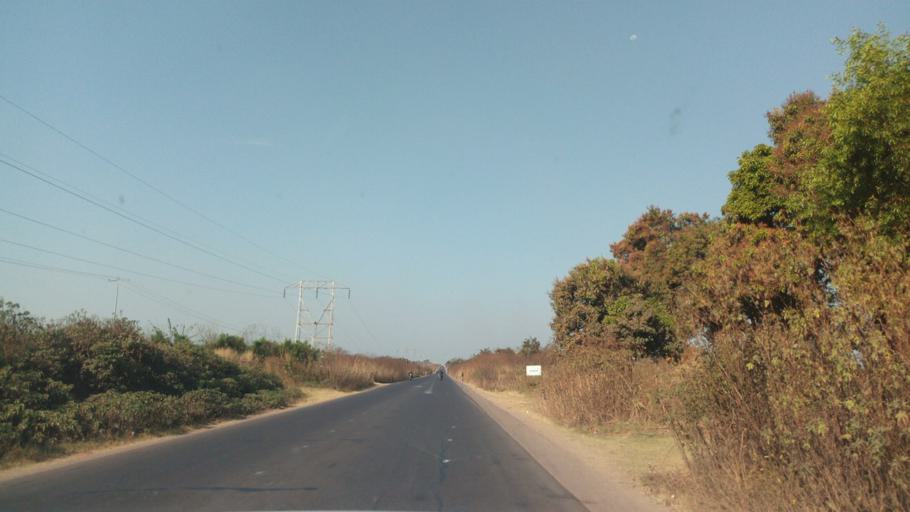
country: CD
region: Katanga
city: Likasi
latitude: -11.0026
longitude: 26.8522
